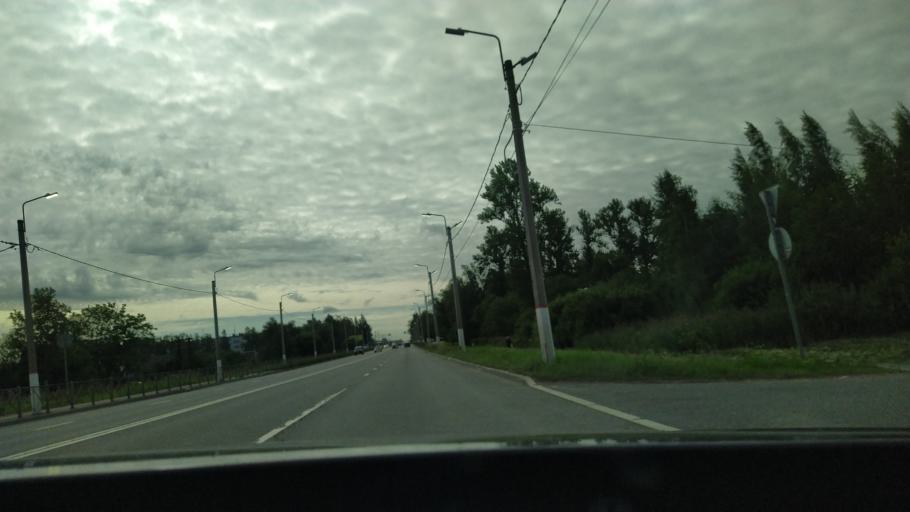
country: RU
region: Leningrad
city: Tosno
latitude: 59.5613
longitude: 30.8398
